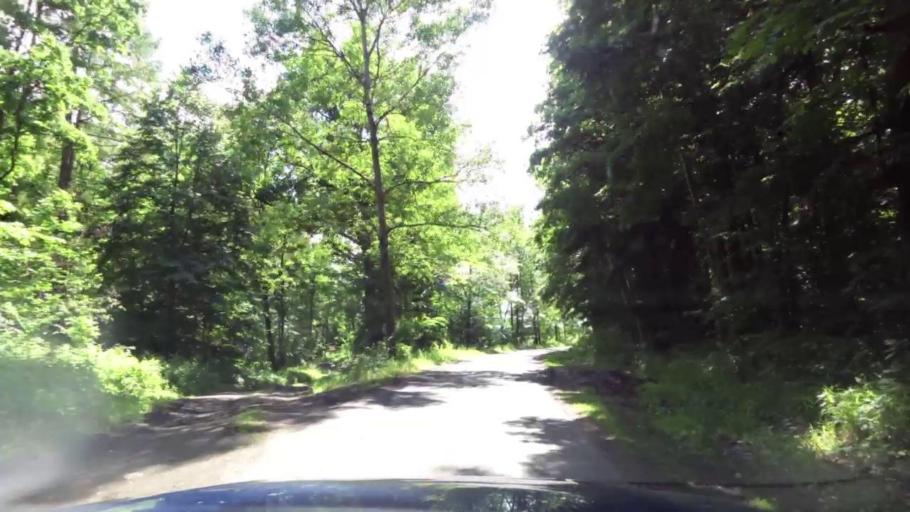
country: PL
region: West Pomeranian Voivodeship
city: Trzcinsko Zdroj
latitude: 52.8899
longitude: 14.6070
